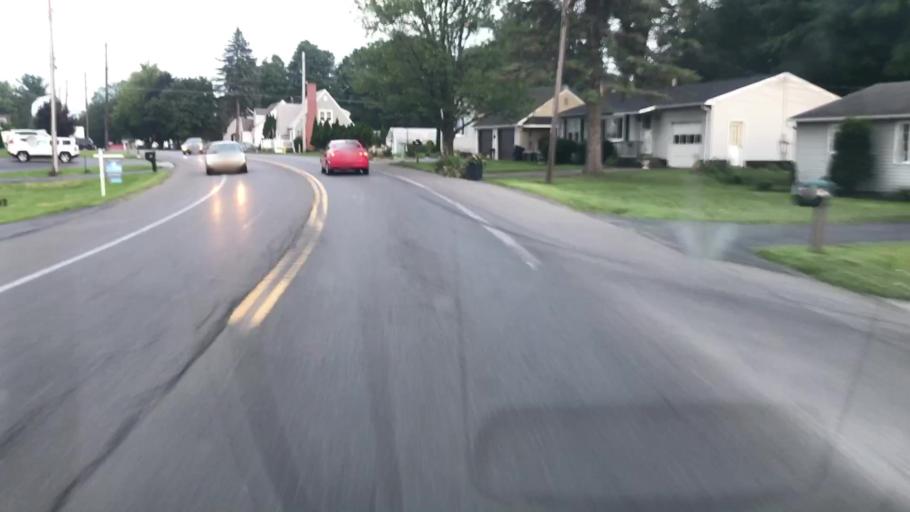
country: US
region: New York
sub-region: Onondaga County
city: North Syracuse
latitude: 43.1421
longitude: -76.1466
